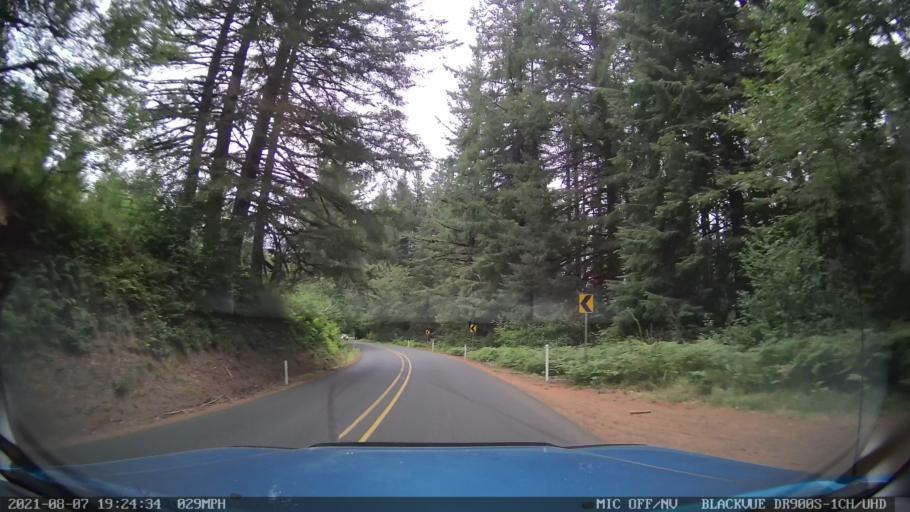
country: US
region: Oregon
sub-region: Linn County
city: Lyons
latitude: 44.8543
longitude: -122.6573
